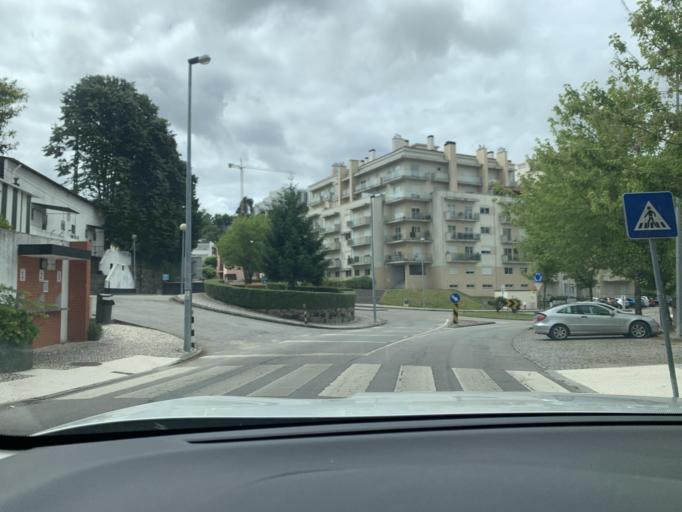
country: PT
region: Viseu
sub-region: Viseu
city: Viseu
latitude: 40.6586
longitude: -7.9264
